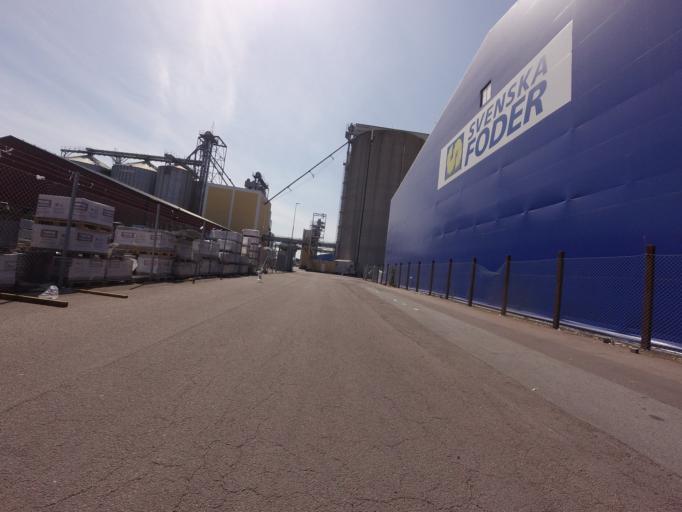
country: SE
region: Skane
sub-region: Landskrona
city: Landskrona
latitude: 55.8636
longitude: 12.8295
